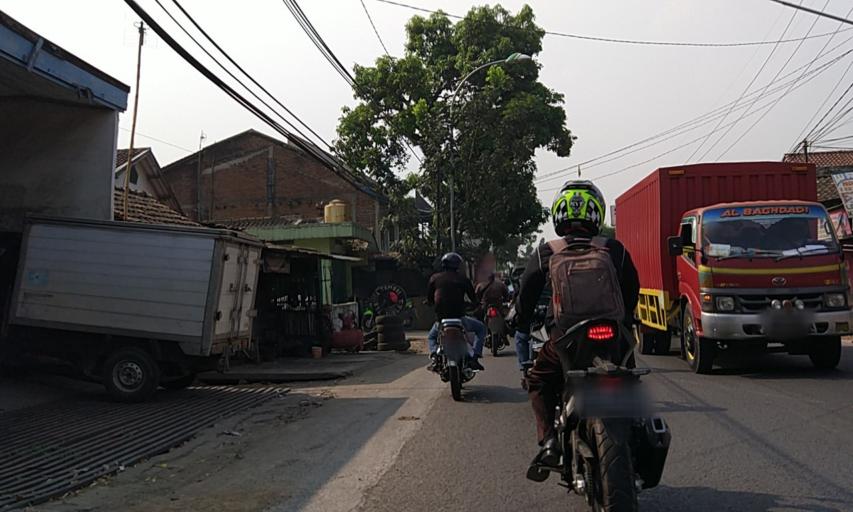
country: ID
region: West Java
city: Soreang
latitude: -7.0156
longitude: 107.5486
